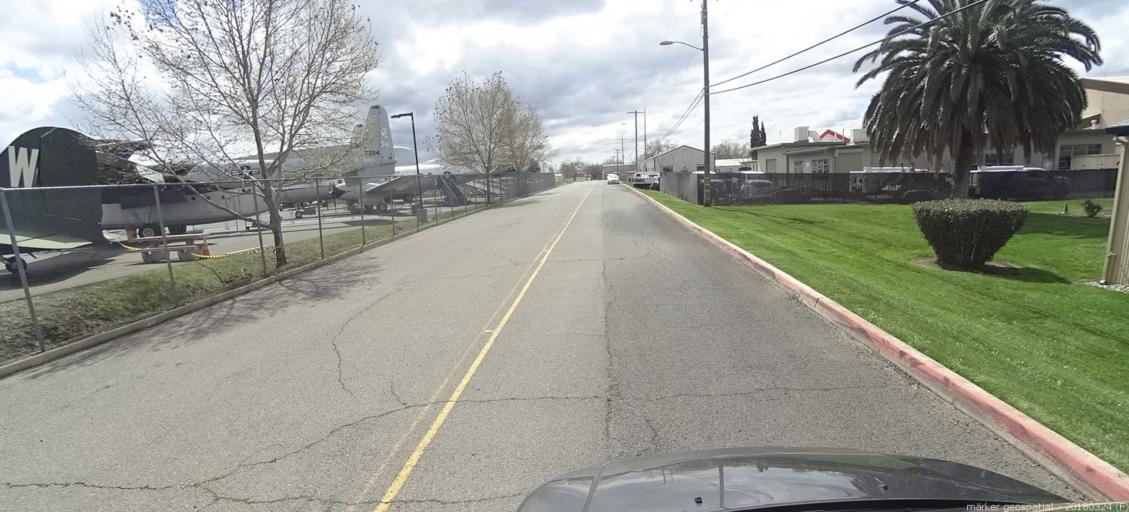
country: US
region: California
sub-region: Sacramento County
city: North Highlands
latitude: 38.6750
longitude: -121.3922
